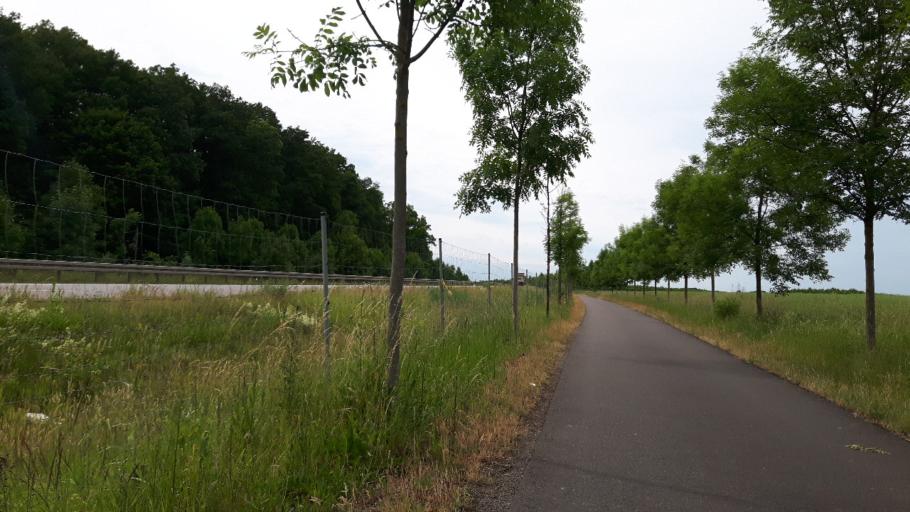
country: DE
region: Saxony
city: Rackwitz
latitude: 51.4036
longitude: 12.3295
